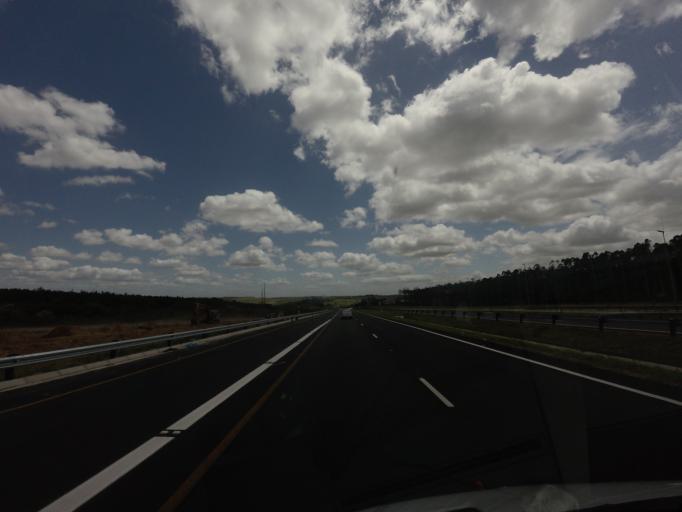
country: ZA
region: KwaZulu-Natal
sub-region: uThungulu District Municipality
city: KwaMbonambi
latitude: -28.5123
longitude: 32.1376
